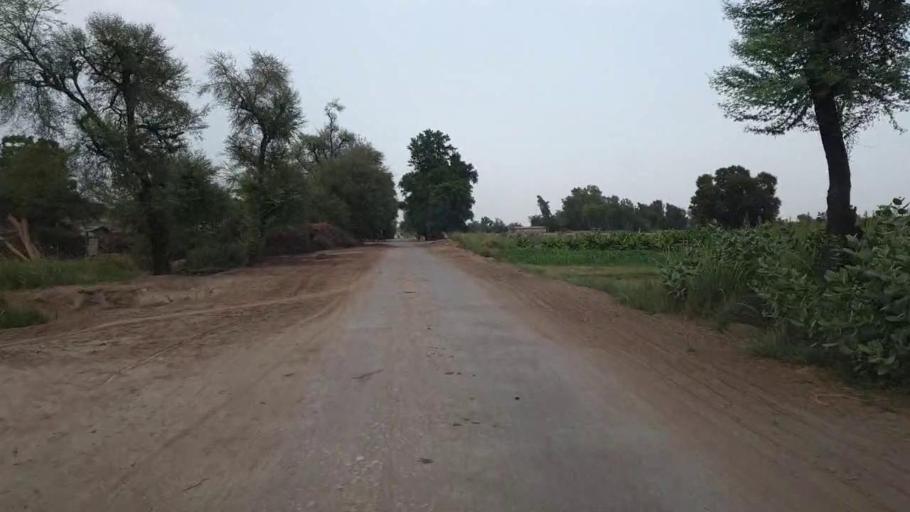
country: PK
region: Sindh
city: Bandhi
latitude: 26.5311
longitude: 68.1986
